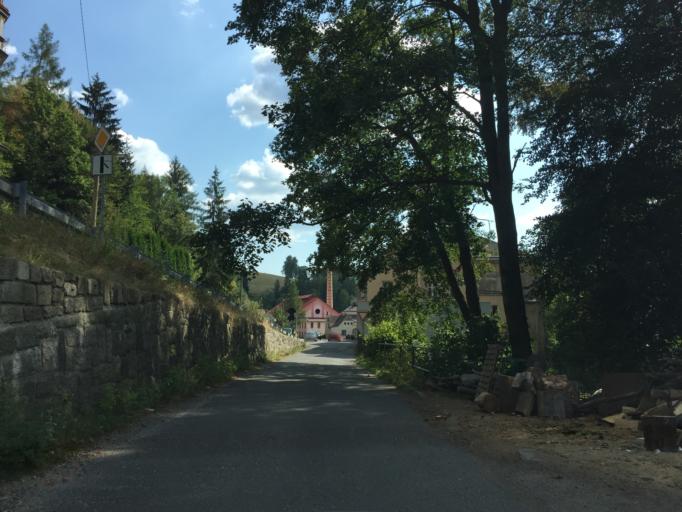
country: CZ
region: Liberecky
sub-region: Okres Jablonec nad Nisou
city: Janov nad Nisou
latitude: 50.7705
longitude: 15.1687
